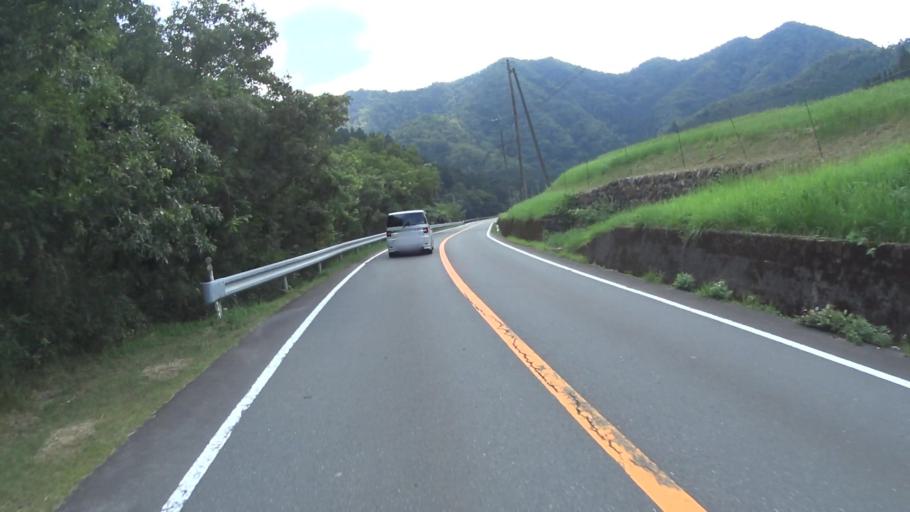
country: JP
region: Kyoto
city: Maizuru
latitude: 35.2907
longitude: 135.5572
